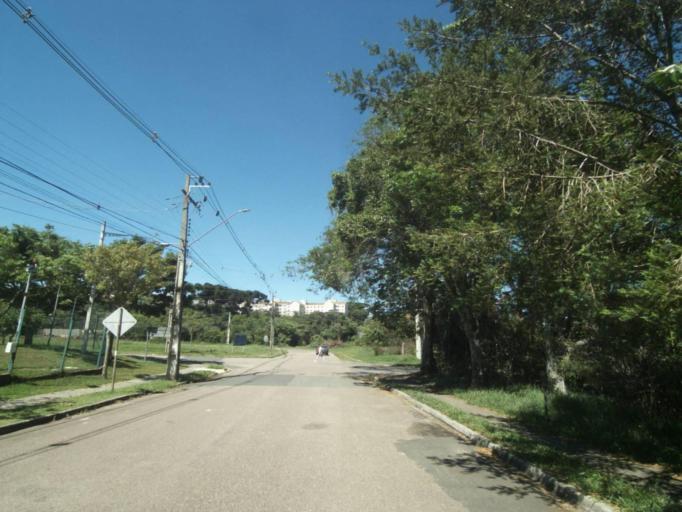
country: BR
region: Parana
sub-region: Curitiba
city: Curitiba
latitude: -25.4716
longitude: -49.3474
